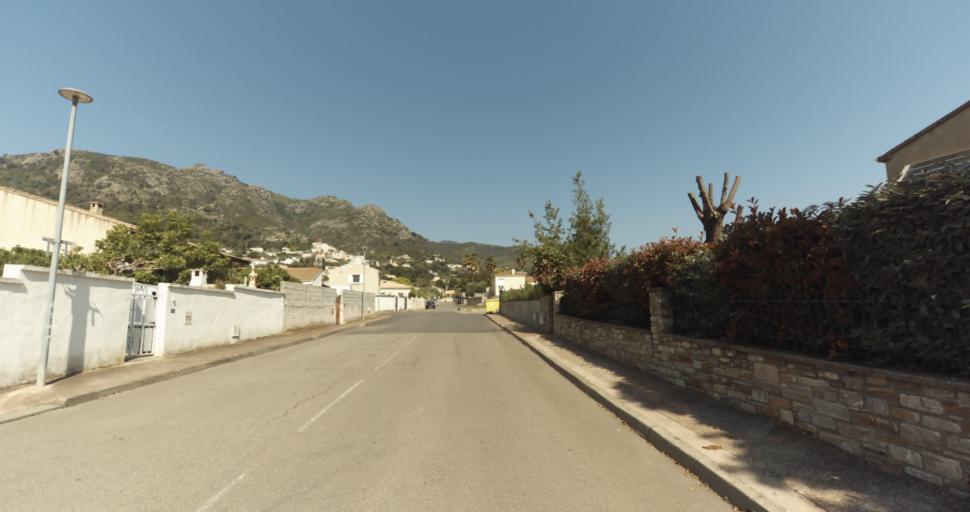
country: FR
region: Corsica
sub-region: Departement de la Haute-Corse
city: Biguglia
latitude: 42.6249
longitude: 9.4286
